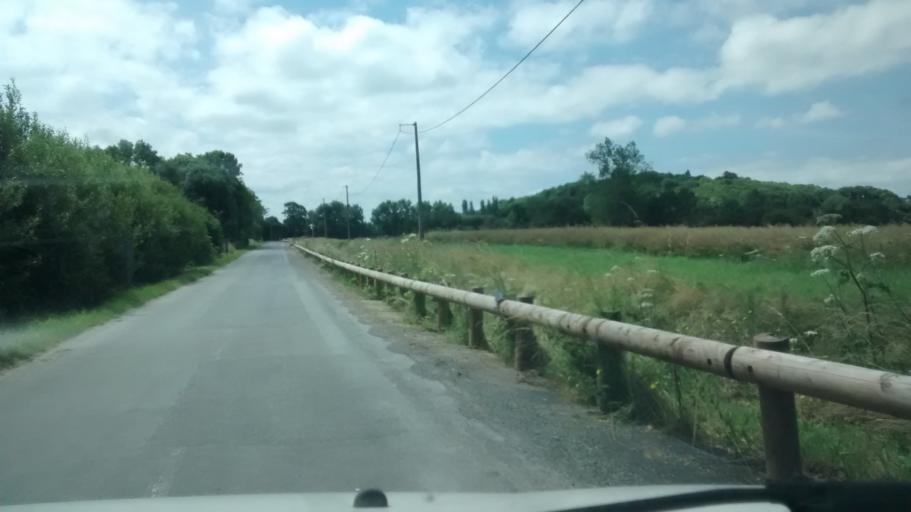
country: FR
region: Brittany
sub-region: Departement d'Ille-et-Vilaine
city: La Gouesniere
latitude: 48.6108
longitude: -1.8839
